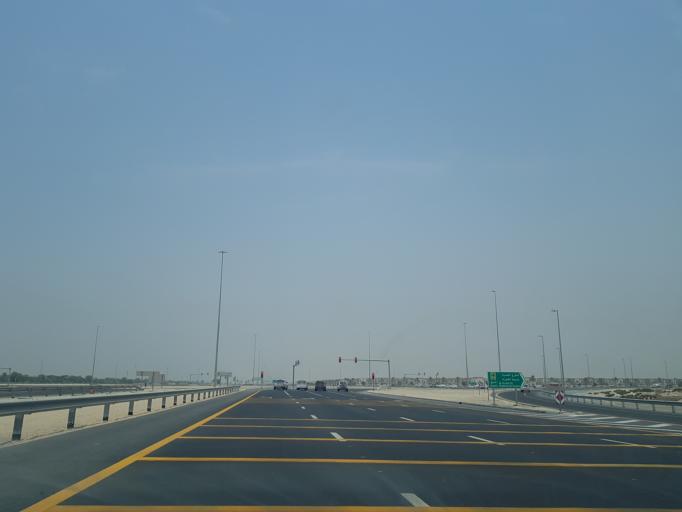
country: AE
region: Dubai
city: Dubai
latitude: 25.0343
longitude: 55.2582
